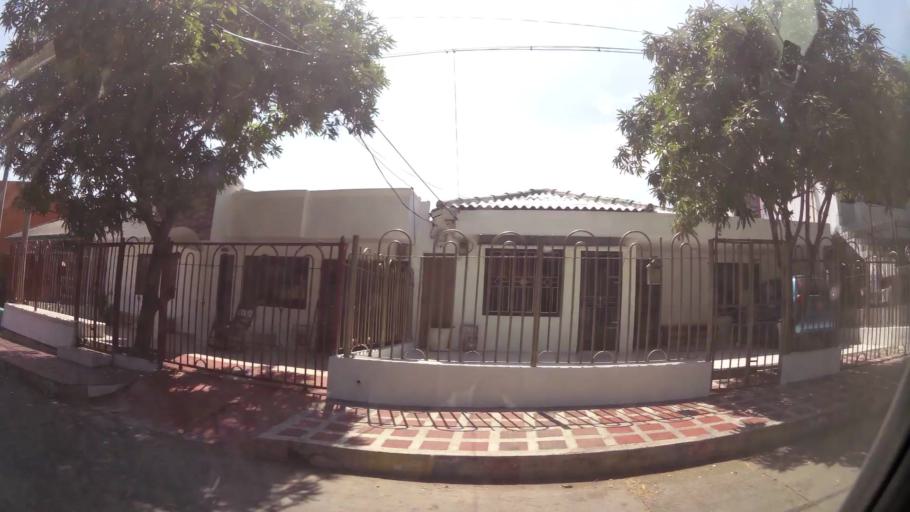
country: CO
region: Atlantico
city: Barranquilla
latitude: 10.9764
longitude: -74.8088
